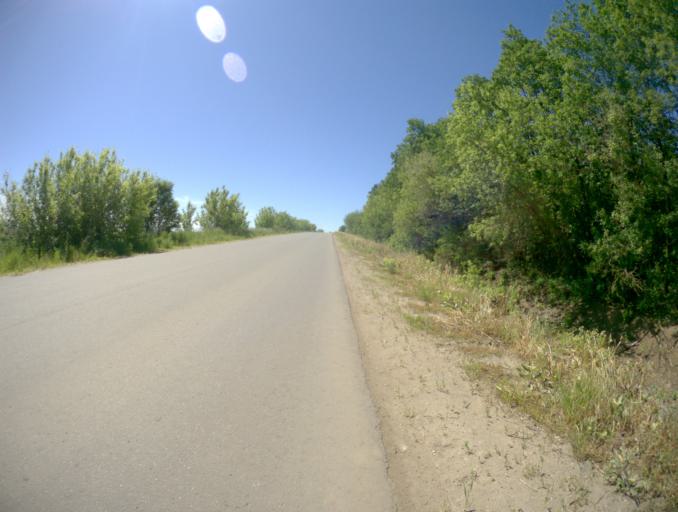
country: RU
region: Ivanovo
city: Gavrilov Posad
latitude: 56.5649
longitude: 40.0356
